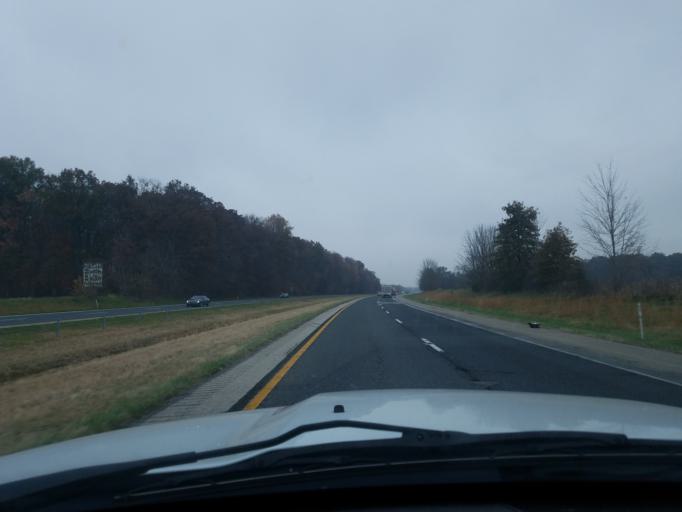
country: US
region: Indiana
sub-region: Bartholomew County
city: Columbus
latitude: 39.1186
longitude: -85.9573
